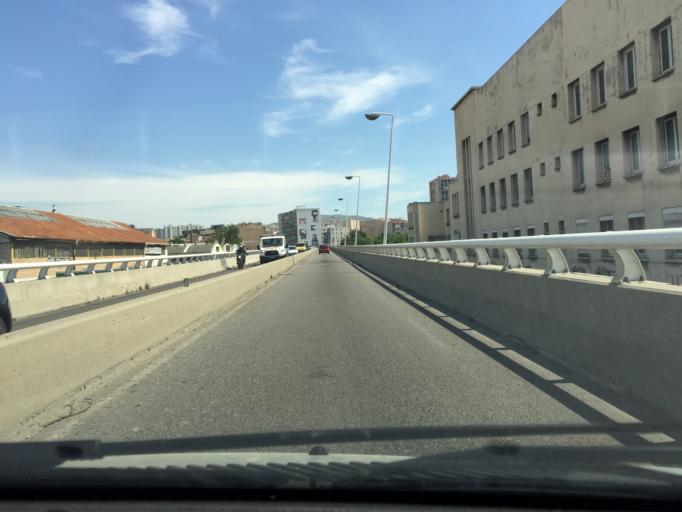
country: FR
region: Provence-Alpes-Cote d'Azur
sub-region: Departement des Bouches-du-Rhone
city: Marseille 03
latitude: 43.3184
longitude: 5.3798
